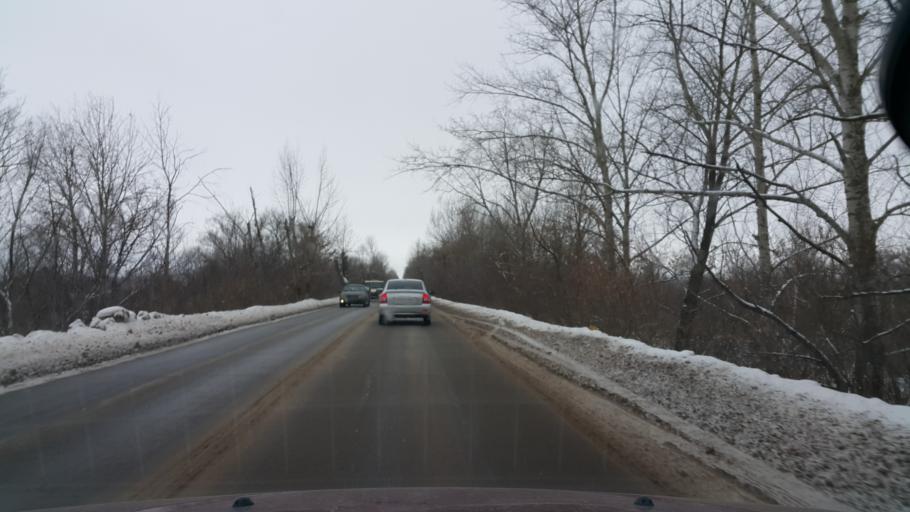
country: RU
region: Tambov
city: Kotovsk
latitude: 52.5861
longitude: 41.4859
